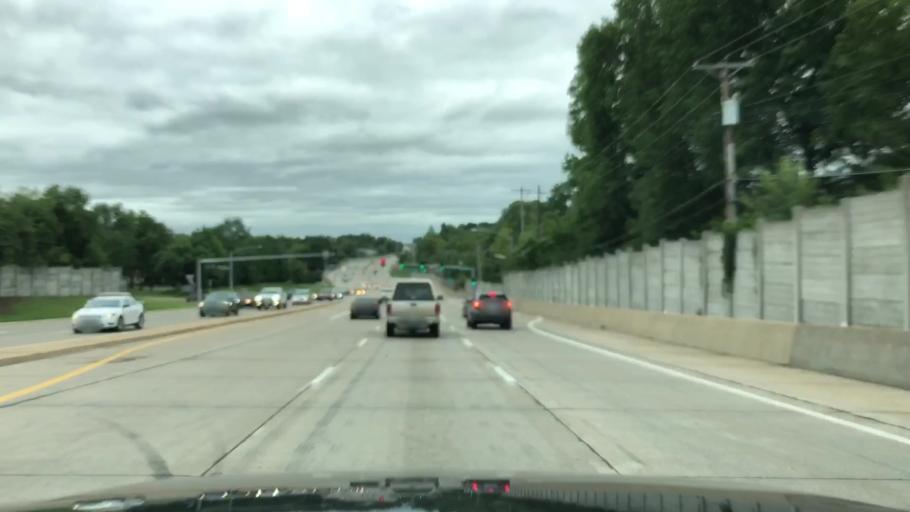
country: US
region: Missouri
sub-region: Saint Louis County
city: Manchester
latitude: 38.6125
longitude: -90.5120
